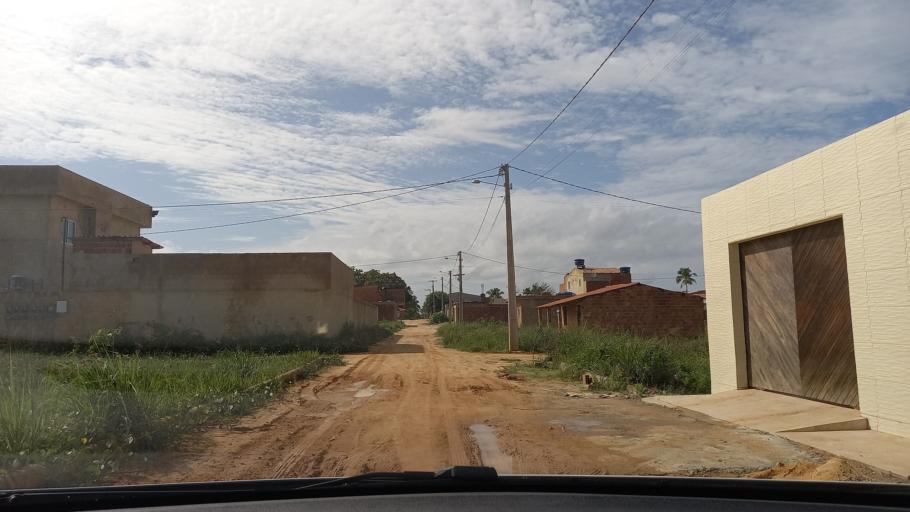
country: BR
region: Pernambuco
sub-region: Sao Jose Da Coroa Grande
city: Sao Jose da Coroa Grande
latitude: -8.9201
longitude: -35.1673
